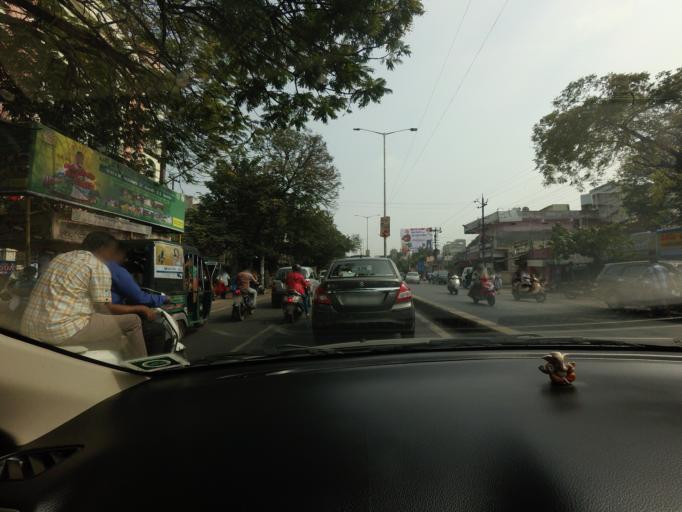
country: IN
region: Andhra Pradesh
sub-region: Krishna
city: Yanamalakuduru
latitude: 16.4930
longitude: 80.6653
